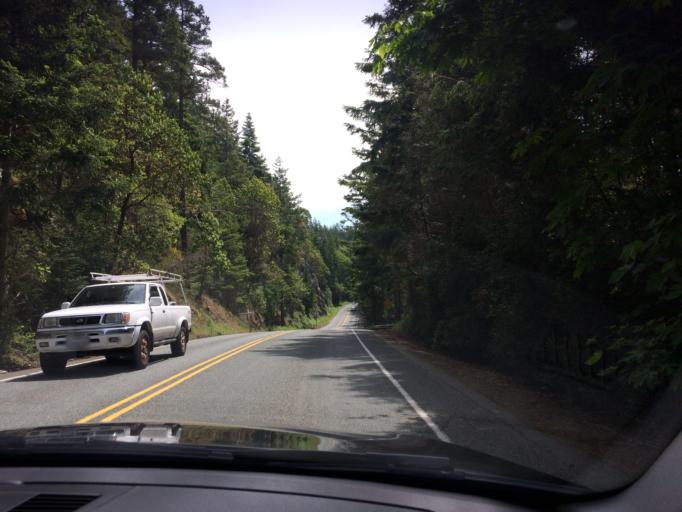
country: US
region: Washington
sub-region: Skagit County
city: Anacortes
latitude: 48.4766
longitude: -122.6597
